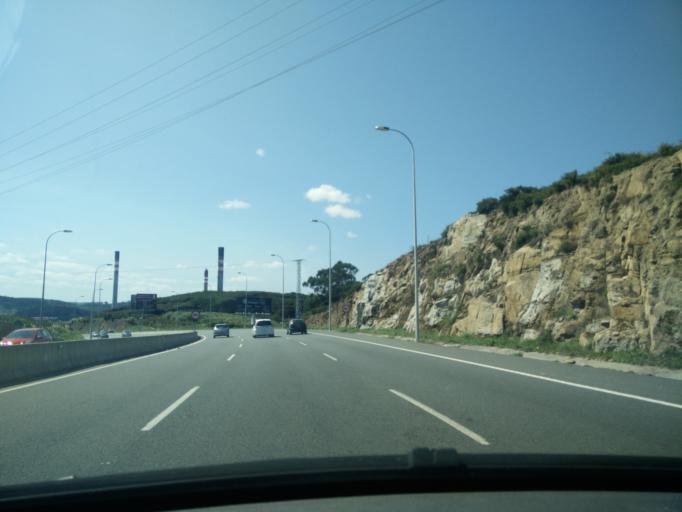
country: ES
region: Galicia
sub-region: Provincia da Coruna
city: A Coruna
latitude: 43.3570
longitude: -8.4359
